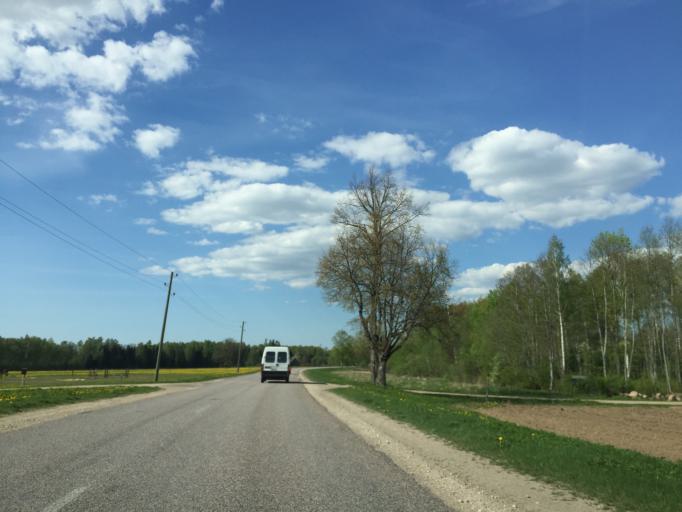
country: LV
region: Limbazu Rajons
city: Limbazi
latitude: 57.4651
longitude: 24.7138
